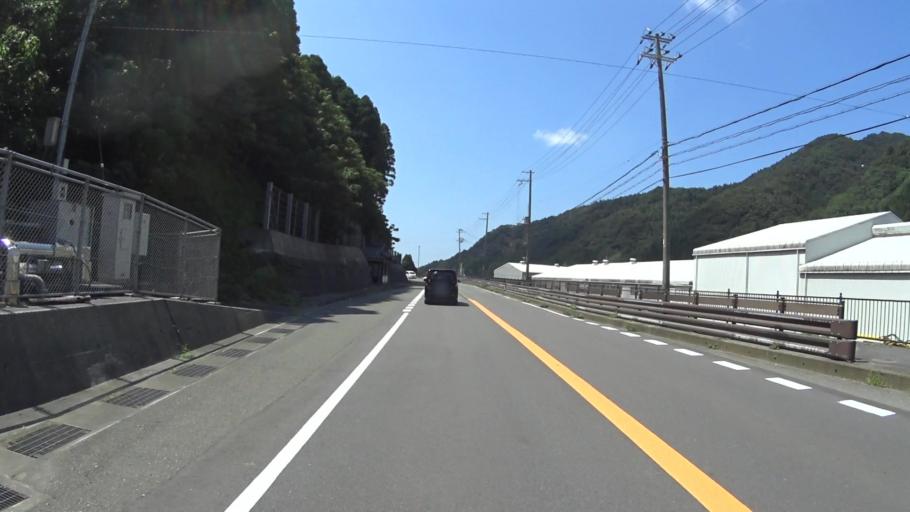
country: JP
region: Fukui
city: Obama
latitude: 35.4478
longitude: 135.8962
